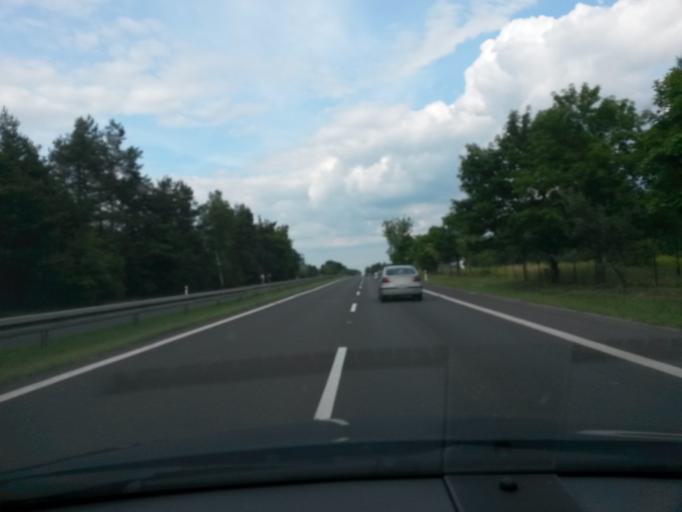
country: PL
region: Lodz Voivodeship
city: Zabia Wola
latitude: 52.0470
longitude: 20.7093
